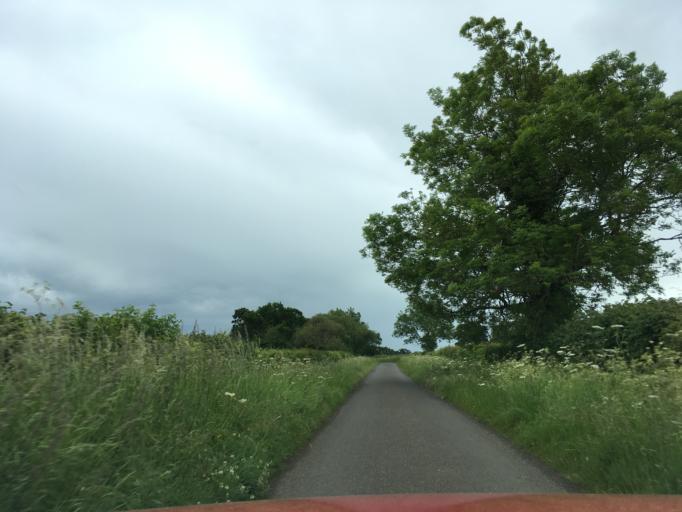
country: GB
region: England
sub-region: Wiltshire
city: Norton
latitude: 51.5887
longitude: -2.2033
